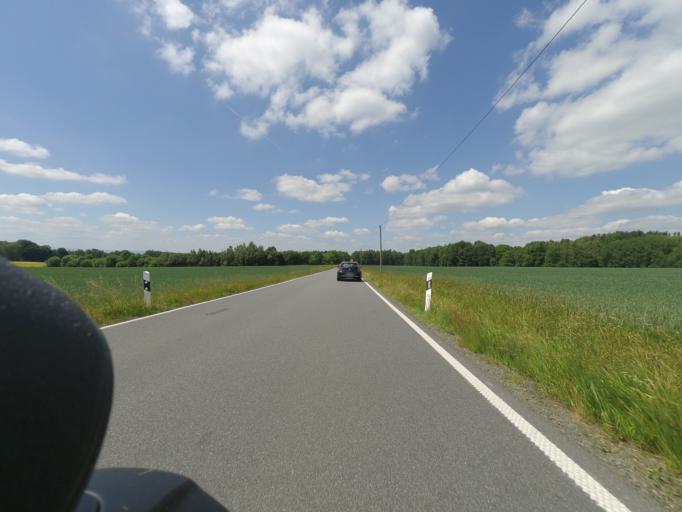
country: DE
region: Saxony
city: Stadt Wehlen
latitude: 50.9880
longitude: 14.0591
